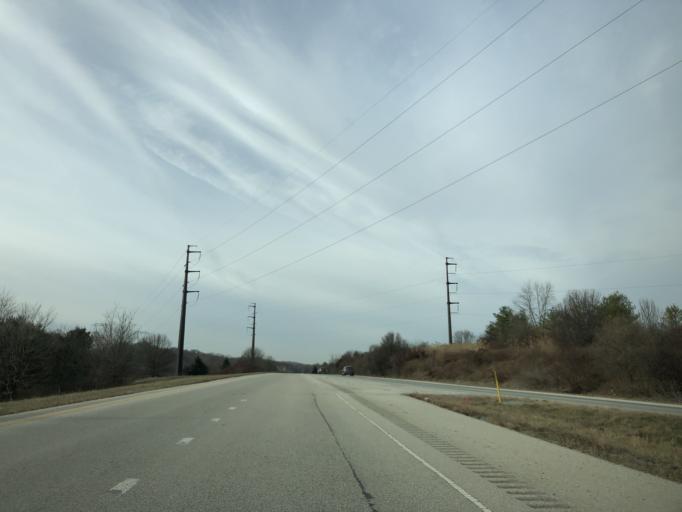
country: US
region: Pennsylvania
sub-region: Chester County
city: Exton
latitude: 40.0303
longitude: -75.5899
